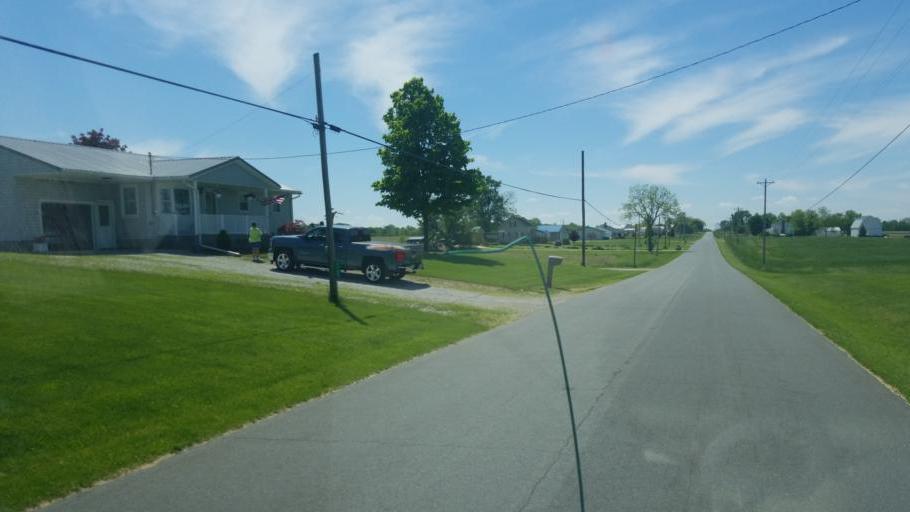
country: US
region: Ohio
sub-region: Huron County
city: Willard
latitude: 41.0833
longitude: -82.7594
